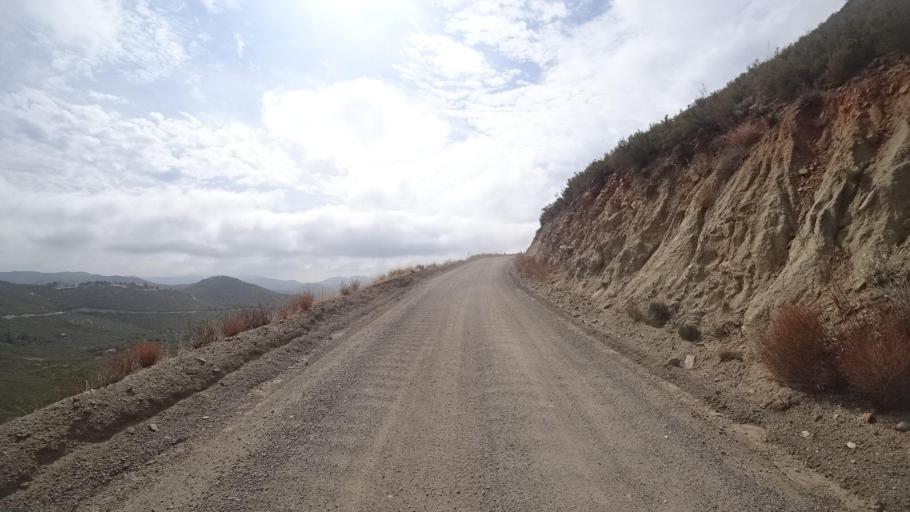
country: US
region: California
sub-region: San Diego County
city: Descanso
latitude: 32.9260
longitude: -116.6324
